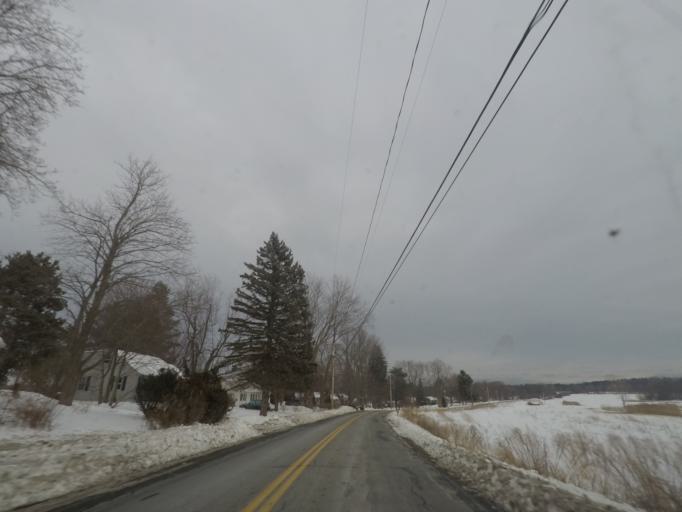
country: US
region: New York
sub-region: Rensselaer County
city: Castleton-on-Hudson
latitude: 42.5141
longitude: -73.7016
